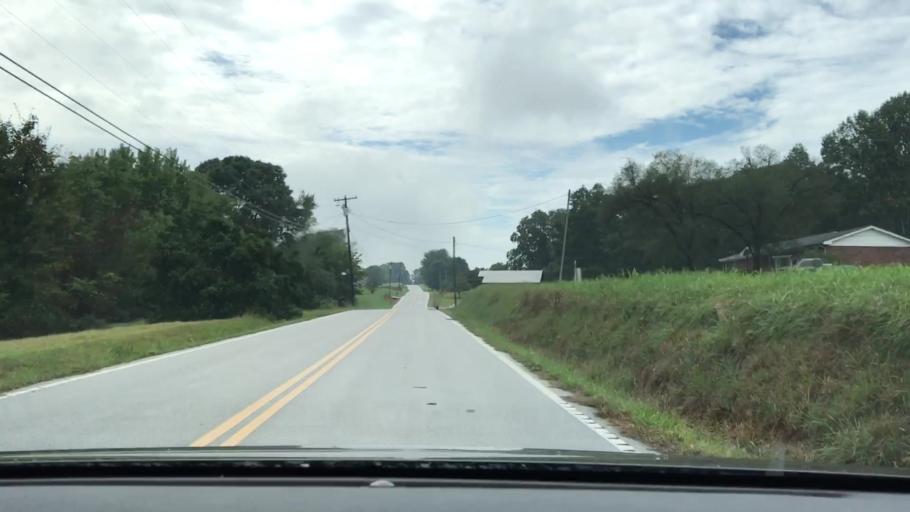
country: US
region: Tennessee
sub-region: Macon County
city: Red Boiling Springs
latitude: 36.4397
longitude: -85.8844
